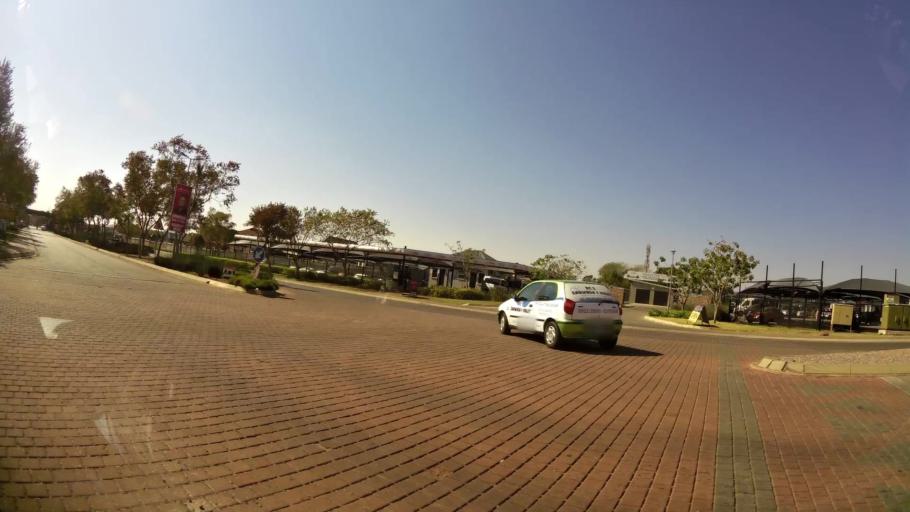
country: ZA
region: Gauteng
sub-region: City of Tshwane Metropolitan Municipality
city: Pretoria
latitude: -25.6798
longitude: 28.2652
